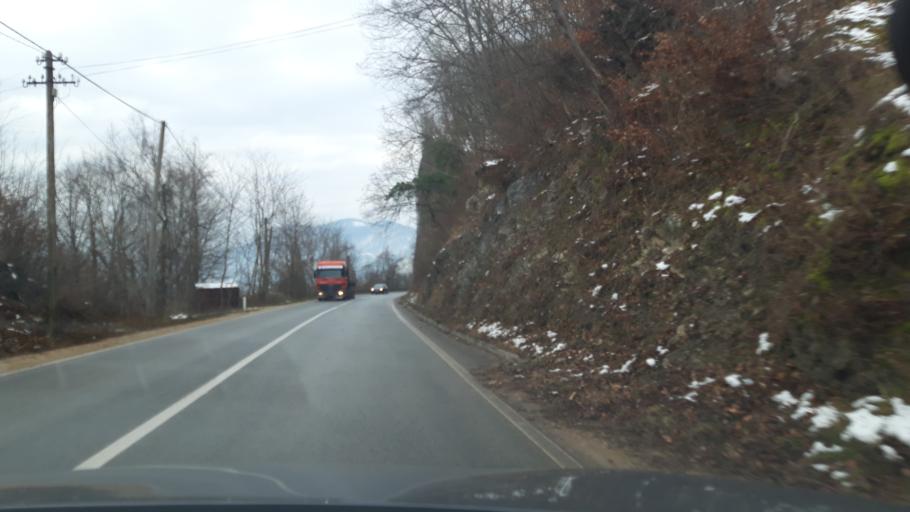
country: RS
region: Central Serbia
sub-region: Macvanski Okrug
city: Mali Zvornik
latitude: 44.3012
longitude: 19.1474
